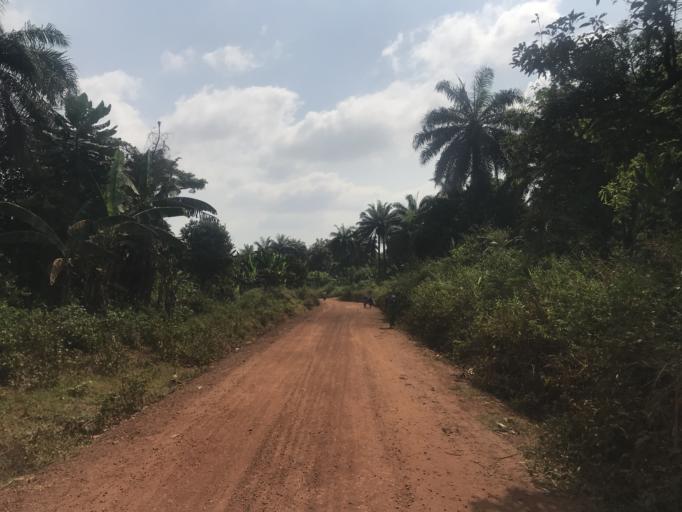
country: NG
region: Osun
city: Ibokun
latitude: 7.8051
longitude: 4.6489
